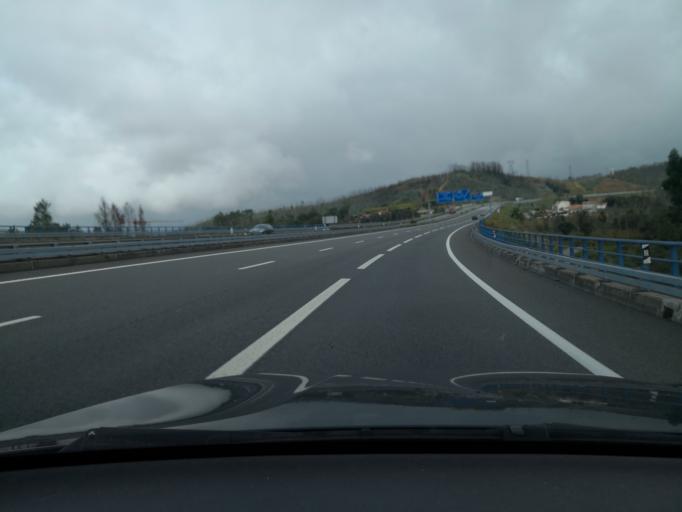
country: PT
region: Porto
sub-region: Valongo
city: Alfena
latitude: 41.2390
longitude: -8.5124
